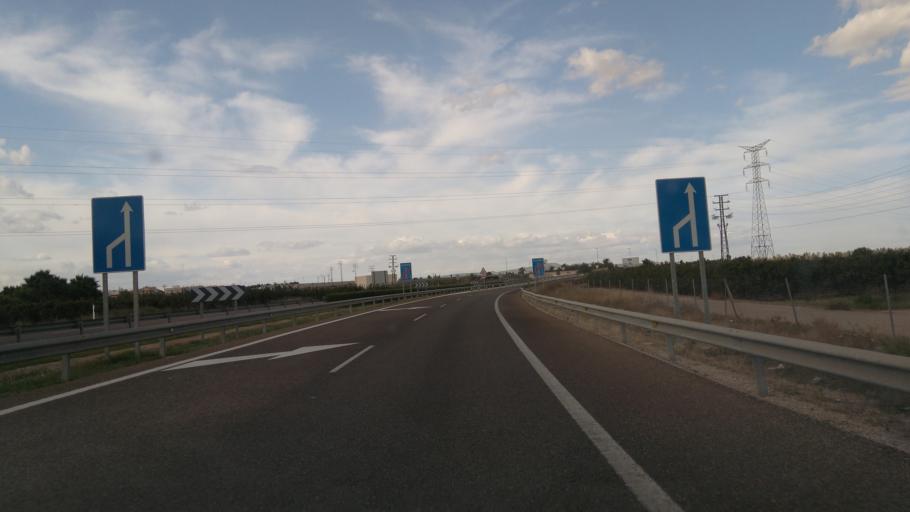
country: ES
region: Valencia
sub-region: Provincia de Valencia
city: L'Alcudia
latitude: 39.1883
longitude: -0.4927
